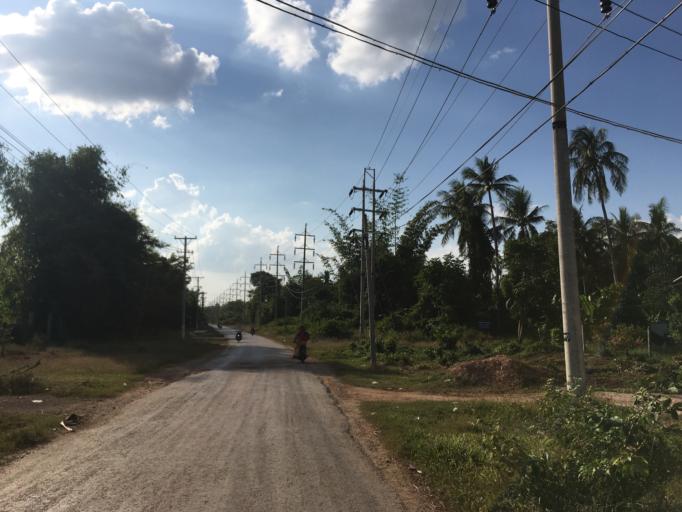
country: MM
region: Mon
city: Mawlamyine
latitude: 16.4283
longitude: 97.6299
